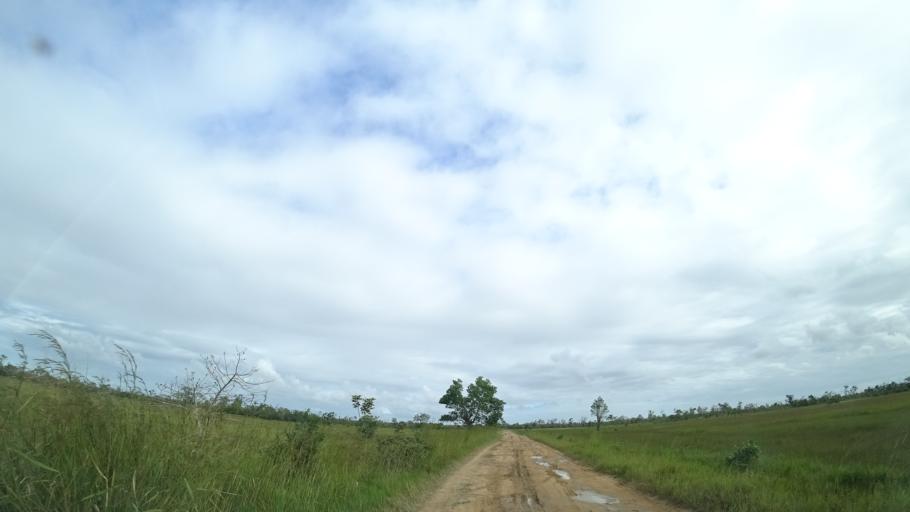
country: MZ
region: Sofala
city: Dondo
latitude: -19.5873
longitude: 35.0862
